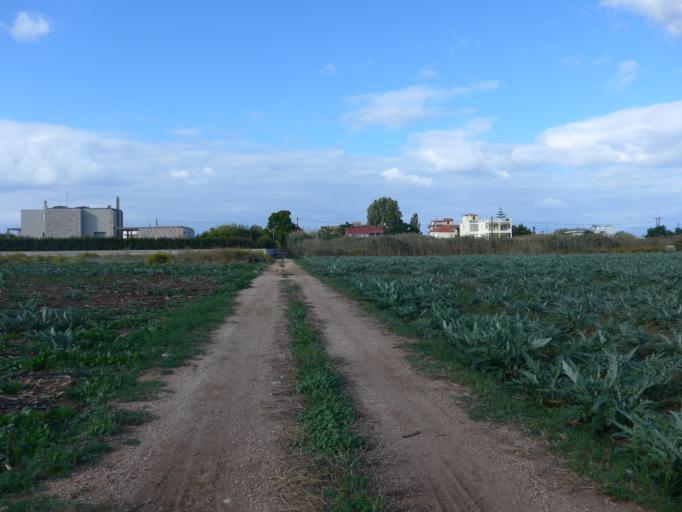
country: GR
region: Peloponnese
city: Asklipieio
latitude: 37.4874
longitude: 22.9952
